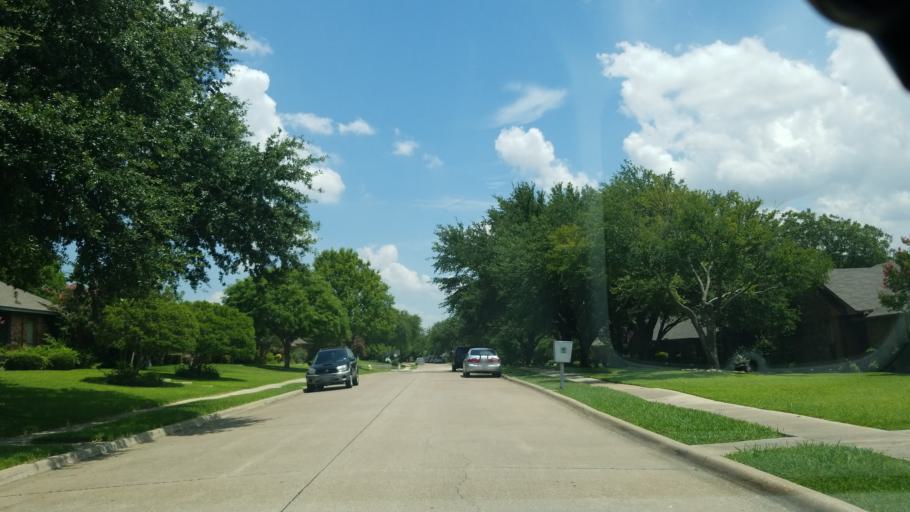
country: US
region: Texas
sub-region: Dallas County
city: Coppell
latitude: 32.9630
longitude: -96.9608
